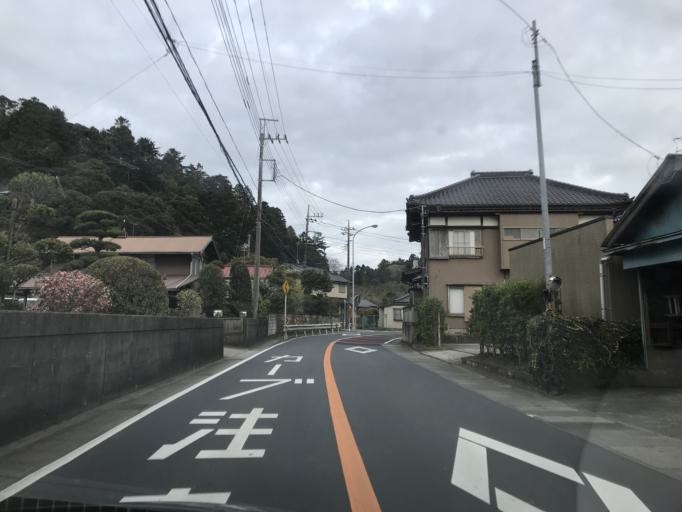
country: JP
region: Chiba
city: Omigawa
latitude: 35.8002
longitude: 140.6072
